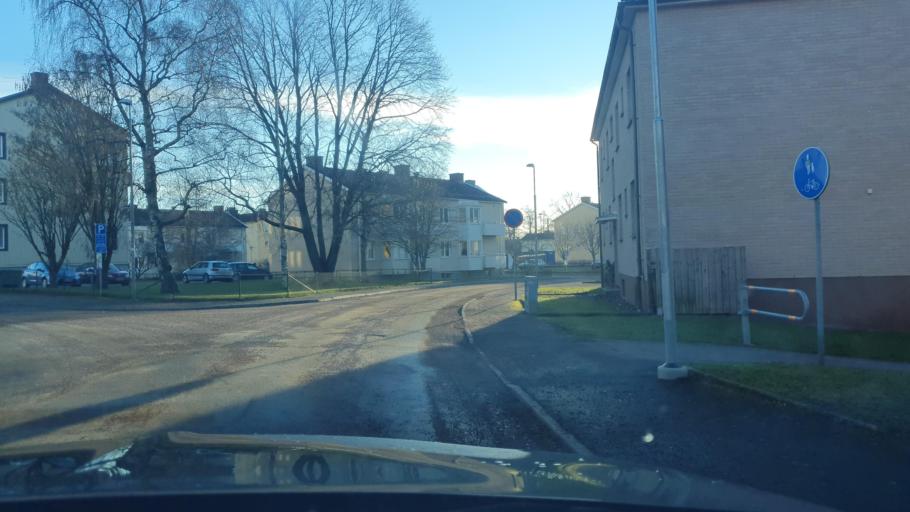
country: SE
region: Vaestra Goetaland
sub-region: Skovde Kommun
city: Skoevde
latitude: 58.3951
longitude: 13.8484
